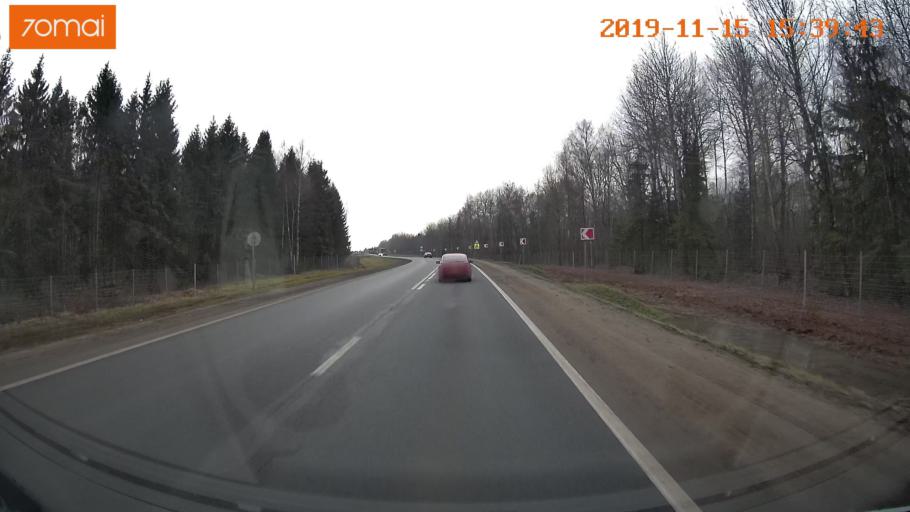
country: RU
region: Jaroslavl
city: Danilov
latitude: 58.0188
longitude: 40.0647
